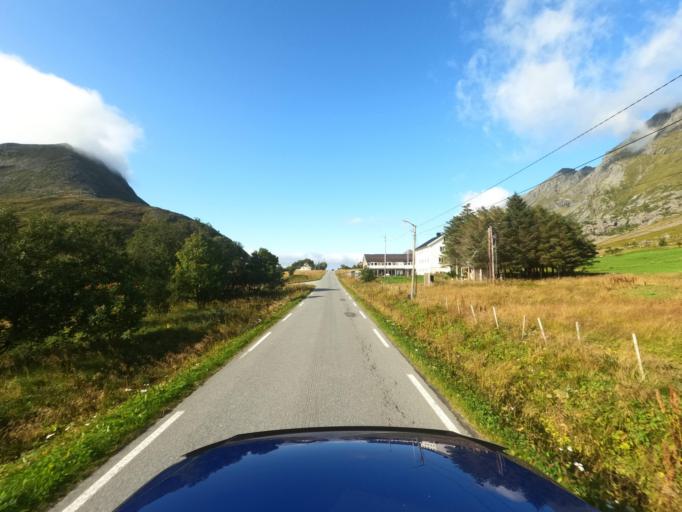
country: NO
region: Nordland
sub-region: Flakstad
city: Ramberg
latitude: 68.0615
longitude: 13.2413
